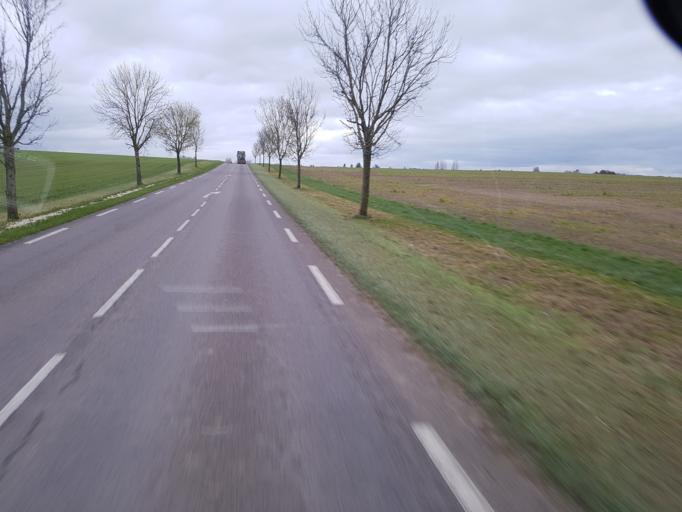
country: FR
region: Champagne-Ardenne
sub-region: Departement de la Marne
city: Sezanne
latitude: 48.6806
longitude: 3.7540
